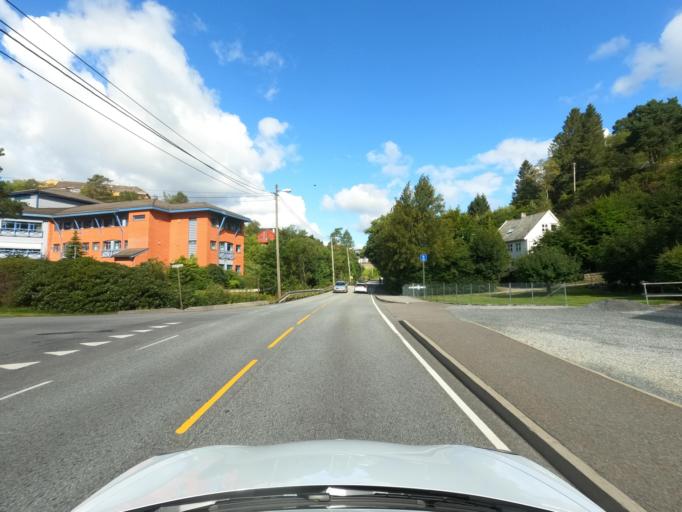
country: NO
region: Hordaland
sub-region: Bergen
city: Bergen
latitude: 60.4495
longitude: 5.3198
